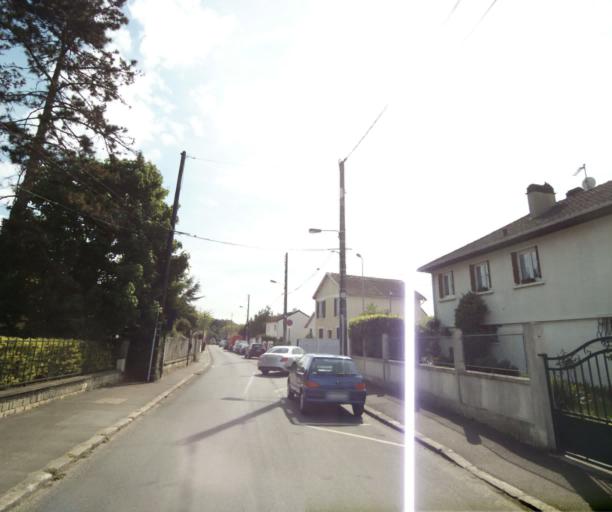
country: FR
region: Ile-de-France
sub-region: Departement des Yvelines
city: Les Mureaux
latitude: 48.9905
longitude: 1.9201
